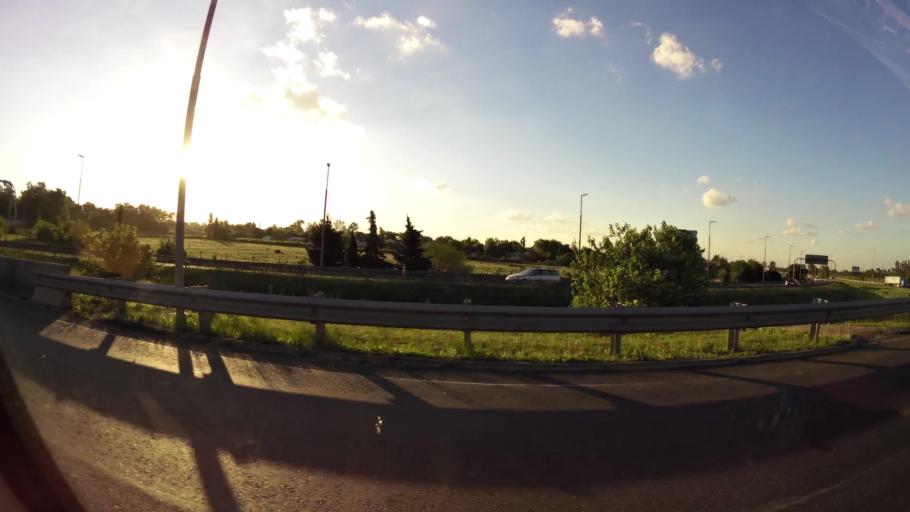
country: AR
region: Buenos Aires
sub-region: Partido de Quilmes
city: Quilmes
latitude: -34.7836
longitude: -58.1530
